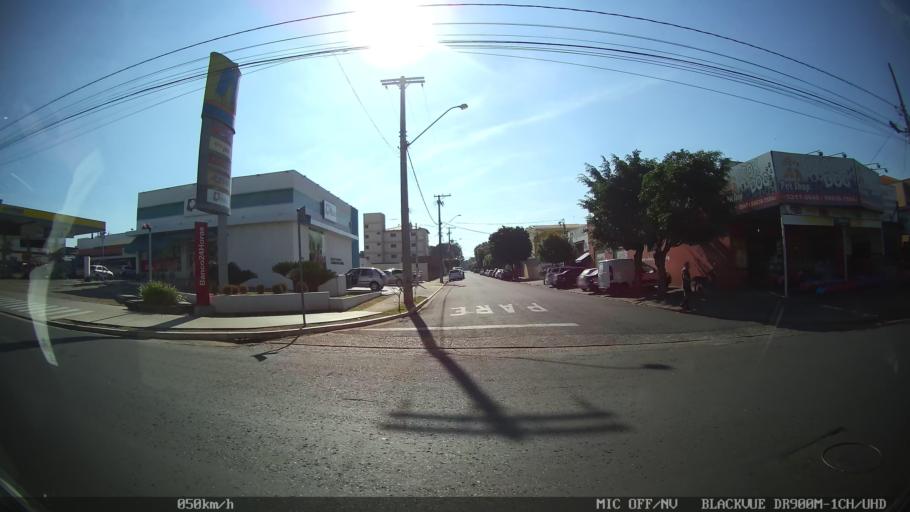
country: BR
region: Sao Paulo
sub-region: Sao Jose Do Rio Preto
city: Sao Jose do Rio Preto
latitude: -20.7984
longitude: -49.4109
